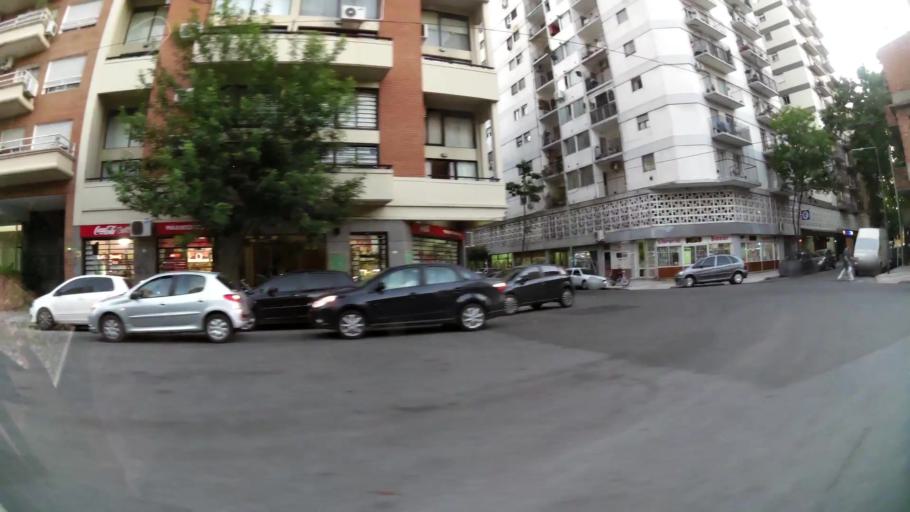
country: AR
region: Buenos Aires F.D.
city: Colegiales
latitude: -34.5490
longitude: -58.4708
